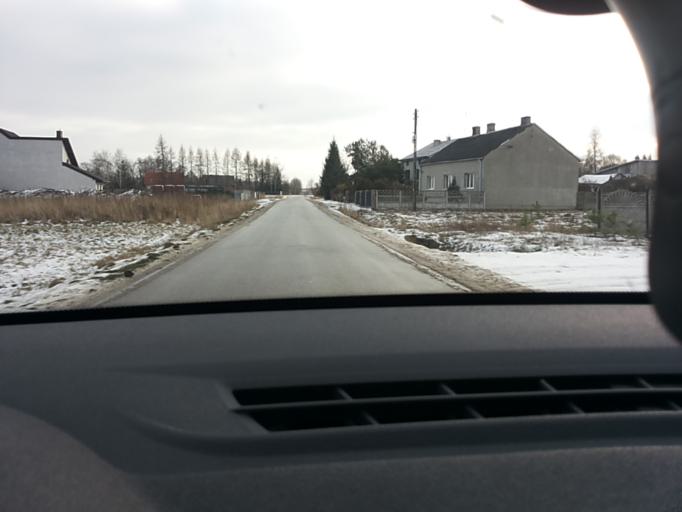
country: PL
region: Lodz Voivodeship
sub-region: Powiat skierniewicki
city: Makow
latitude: 51.9793
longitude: 20.1025
